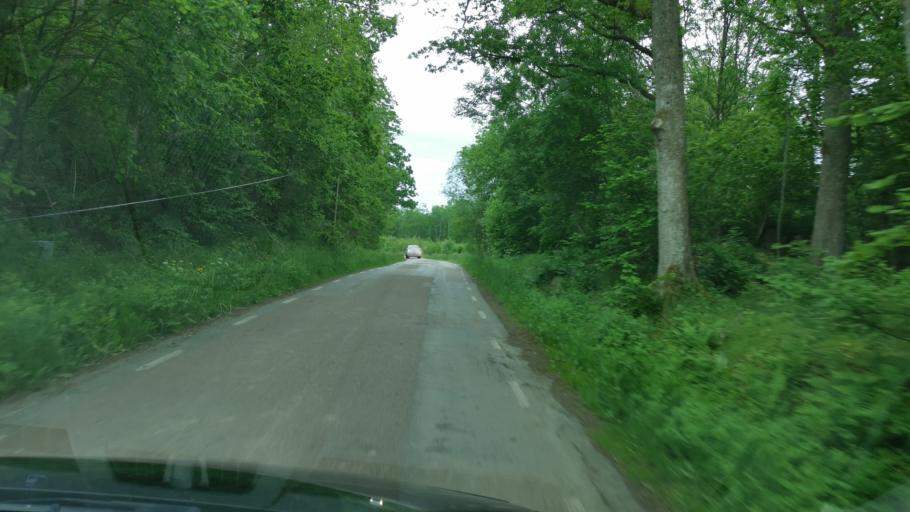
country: SE
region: Vaestra Goetaland
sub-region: Lysekils Kommun
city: Brastad
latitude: 58.3779
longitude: 11.5414
